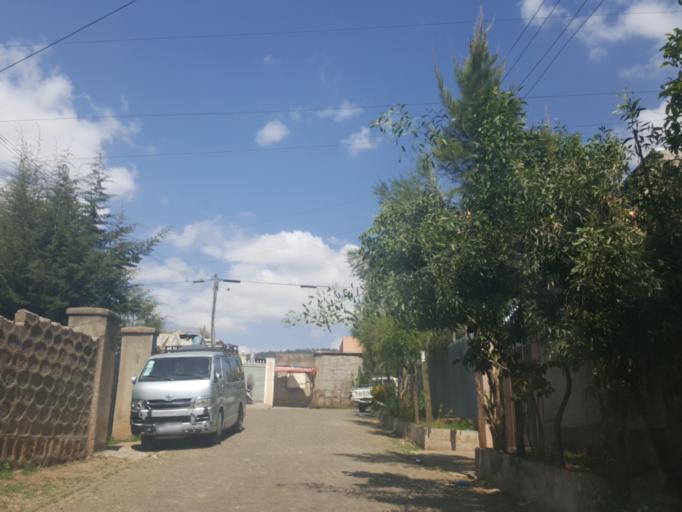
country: ET
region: Adis Abeba
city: Addis Ababa
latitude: 9.0667
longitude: 38.7177
